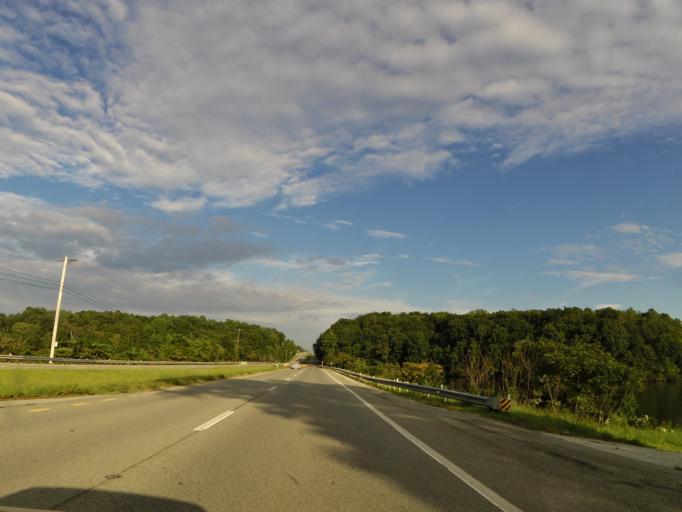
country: US
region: Alabama
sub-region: Lauderdale County
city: Rogersville
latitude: 34.8438
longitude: -87.3727
